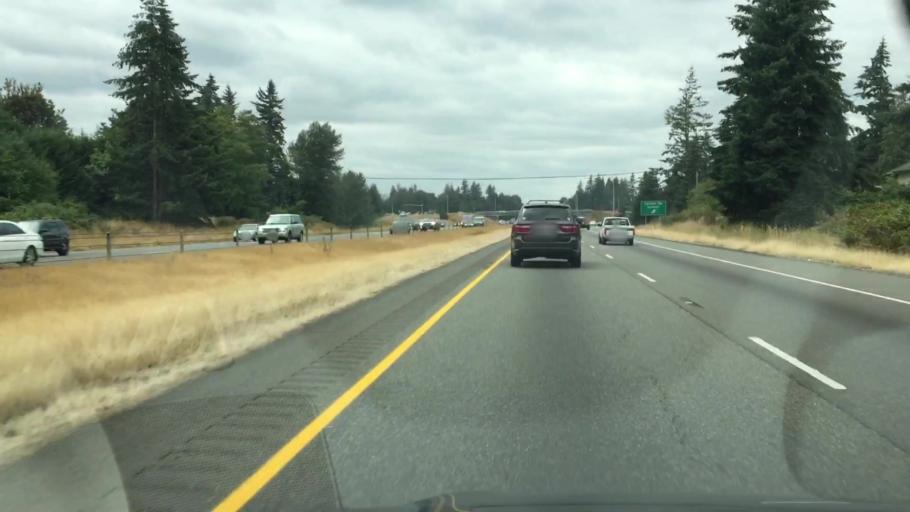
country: US
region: Washington
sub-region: Pierce County
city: Summit
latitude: 47.1578
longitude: -122.3493
